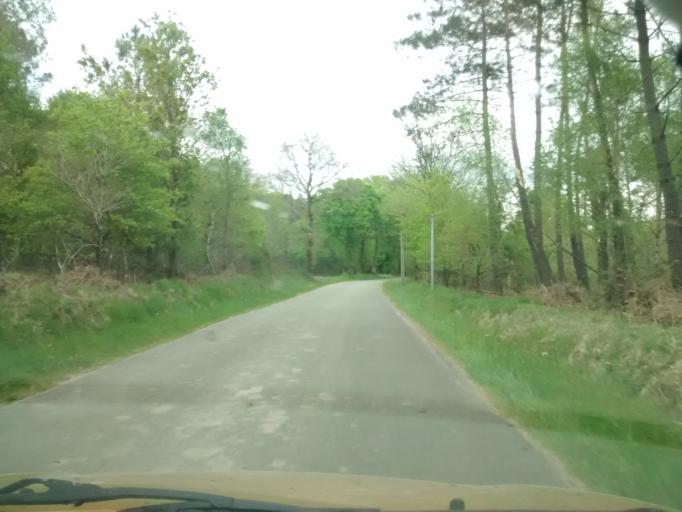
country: FR
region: Brittany
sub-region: Departement du Morbihan
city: Molac
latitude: 47.7429
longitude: -2.4105
